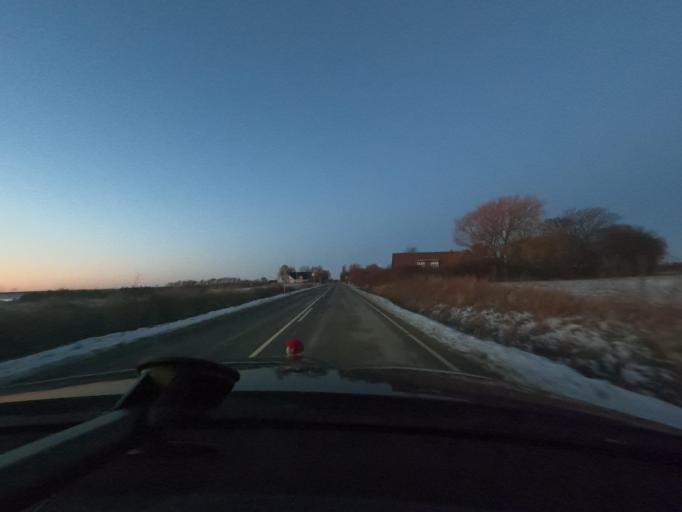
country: DE
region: Schleswig-Holstein
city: Pommerby
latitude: 54.8622
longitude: 9.9984
